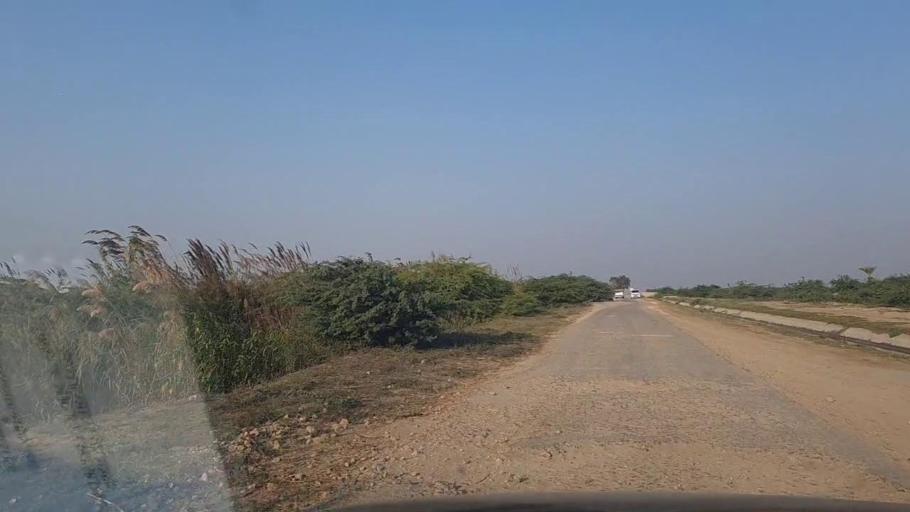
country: PK
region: Sindh
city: Keti Bandar
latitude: 24.2606
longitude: 67.5425
